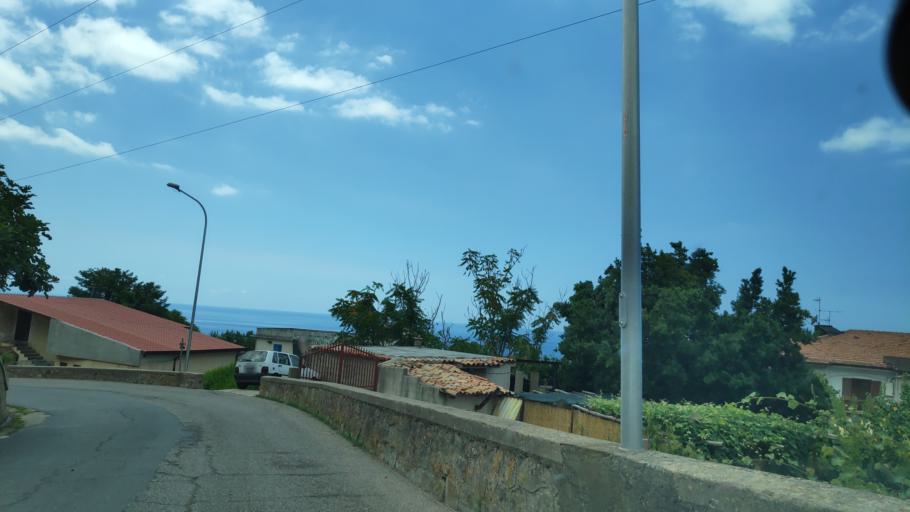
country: IT
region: Calabria
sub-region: Provincia di Cosenza
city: Paola
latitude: 39.3653
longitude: 16.0446
